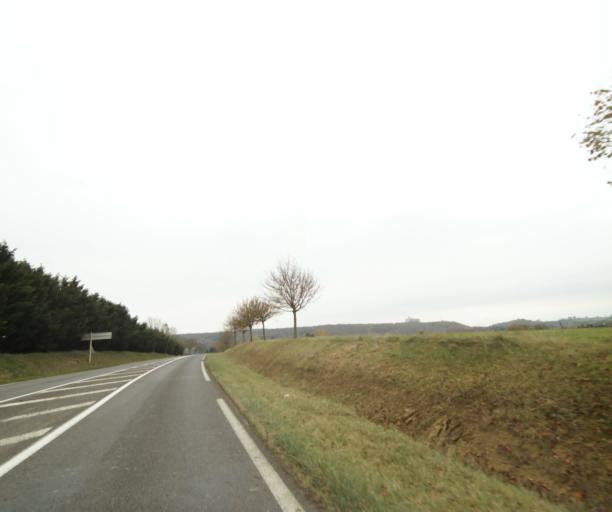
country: FR
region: Lorraine
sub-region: Departement de Meurthe-et-Moselle
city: Mancieulles
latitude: 49.2729
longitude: 5.9132
